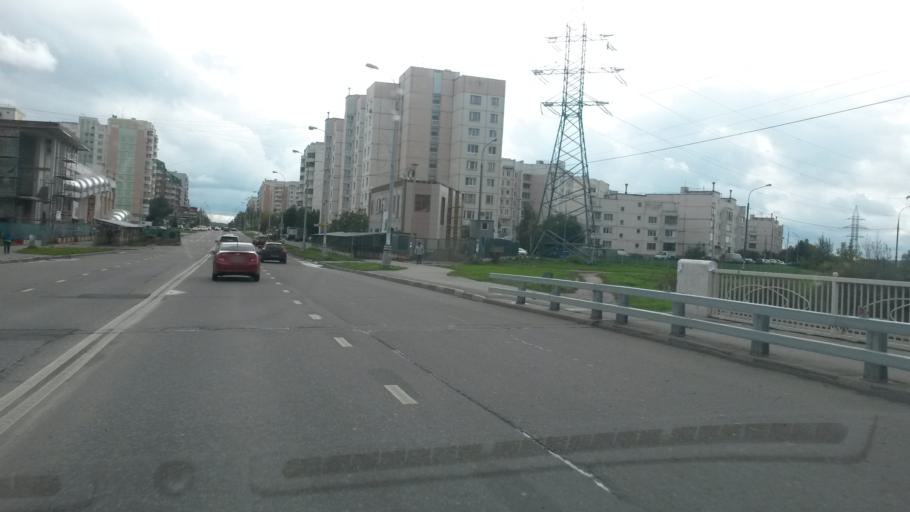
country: RU
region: Moskovskaya
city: Kommunarka
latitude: 55.5368
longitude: 37.5145
